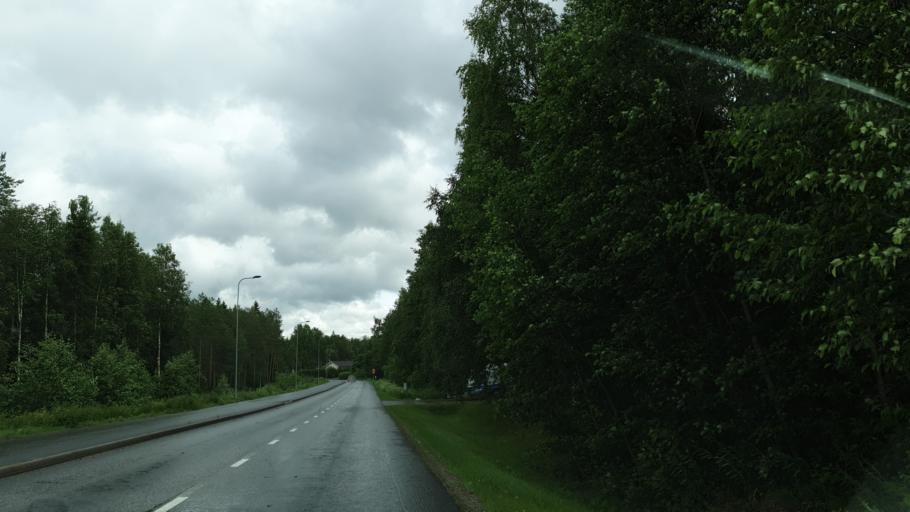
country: FI
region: Kainuu
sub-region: Kehys-Kainuu
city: Kuhmo
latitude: 64.1196
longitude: 29.4920
